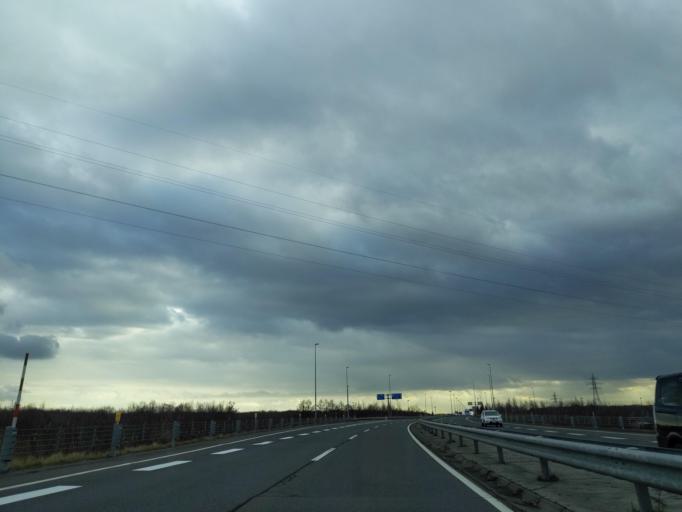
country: JP
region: Hokkaido
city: Chitose
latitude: 42.8284
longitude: 141.6896
